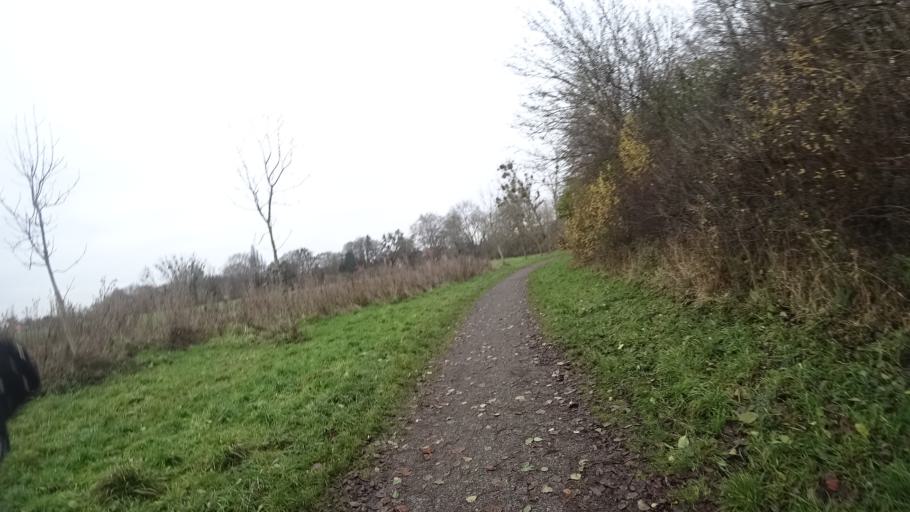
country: DE
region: Lower Saxony
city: Lauenau
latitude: 52.2705
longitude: 9.3651
